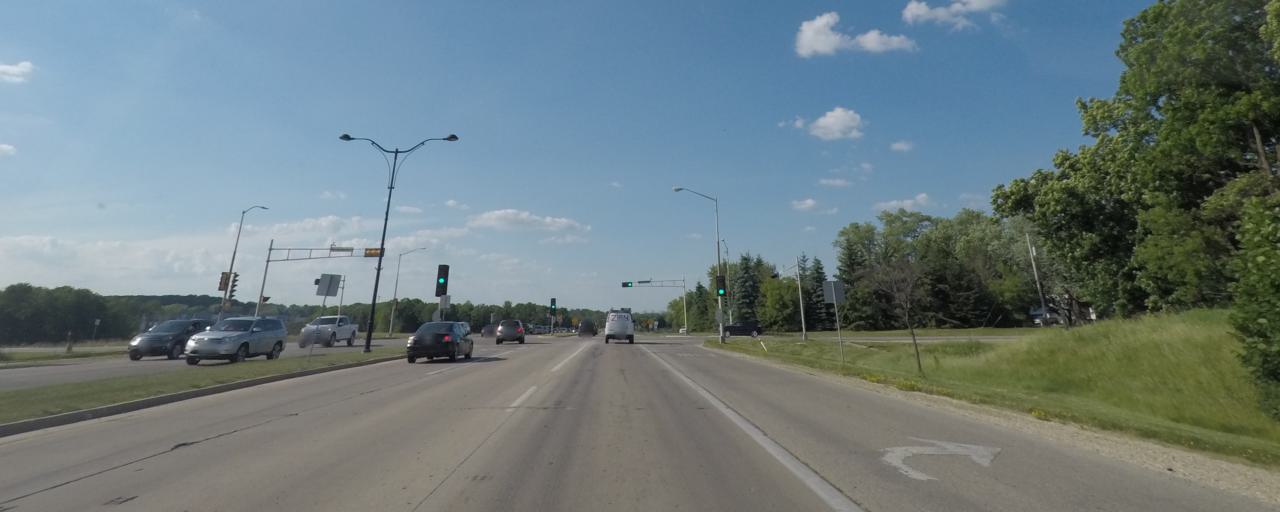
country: US
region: Wisconsin
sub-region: Waukesha County
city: Muskego
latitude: 42.9293
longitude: -88.1141
